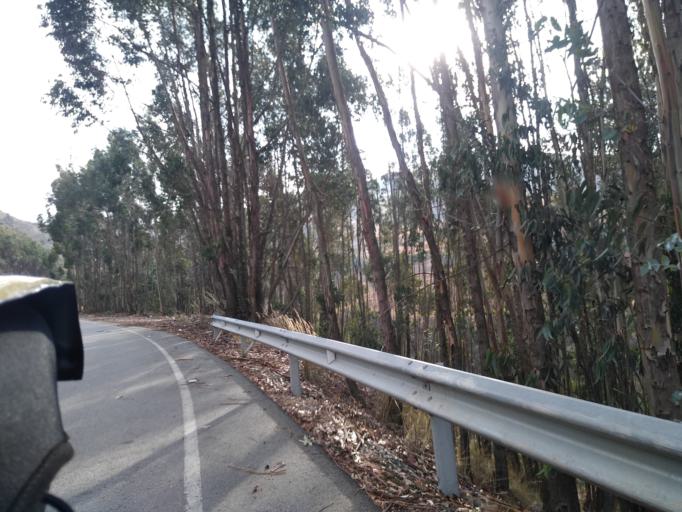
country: PE
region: La Libertad
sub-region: Provincia de Otuzco
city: Agallpampa
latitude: -7.9892
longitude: -78.5318
